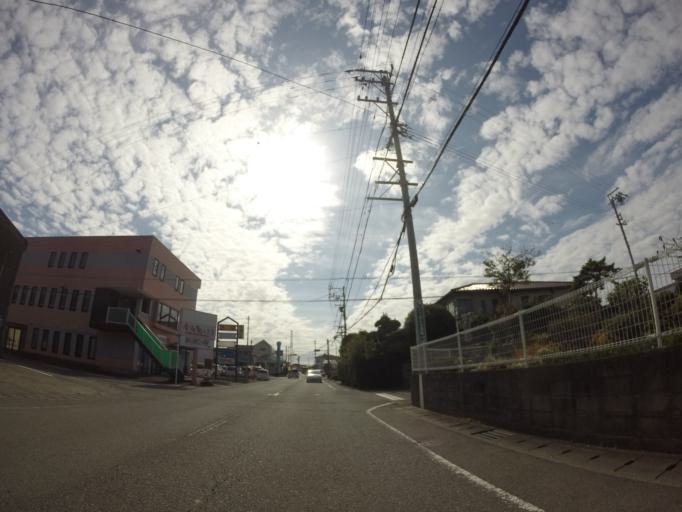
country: JP
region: Shizuoka
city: Yaizu
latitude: 34.8831
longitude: 138.3061
